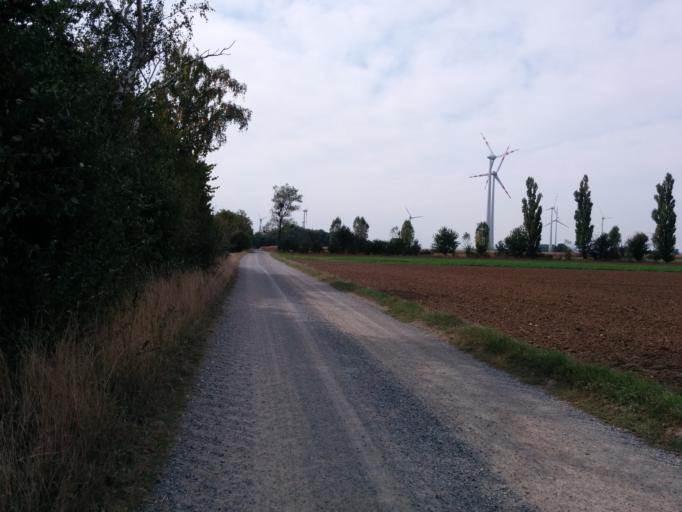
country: AT
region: Lower Austria
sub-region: Politischer Bezirk Bruck an der Leitha
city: Petronell-Carnuntum
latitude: 48.1006
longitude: 16.8593
